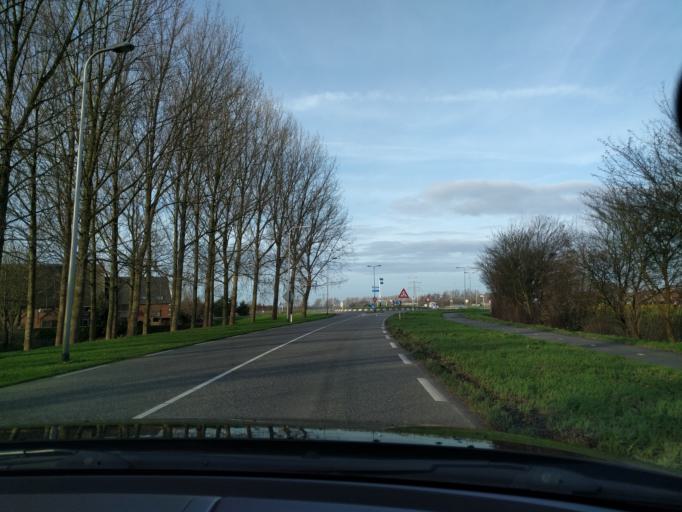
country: NL
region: South Holland
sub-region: Gemeente Spijkenisse
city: Spijkenisse
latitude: 51.8359
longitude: 4.2513
